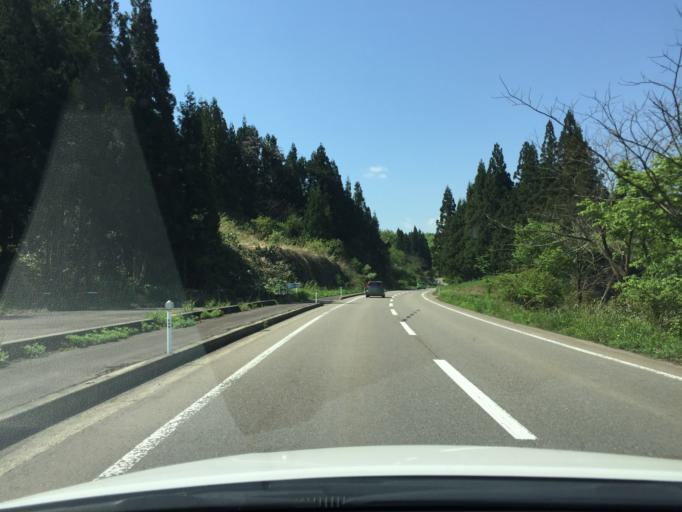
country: JP
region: Niigata
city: Kamo
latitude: 37.5882
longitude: 139.0944
